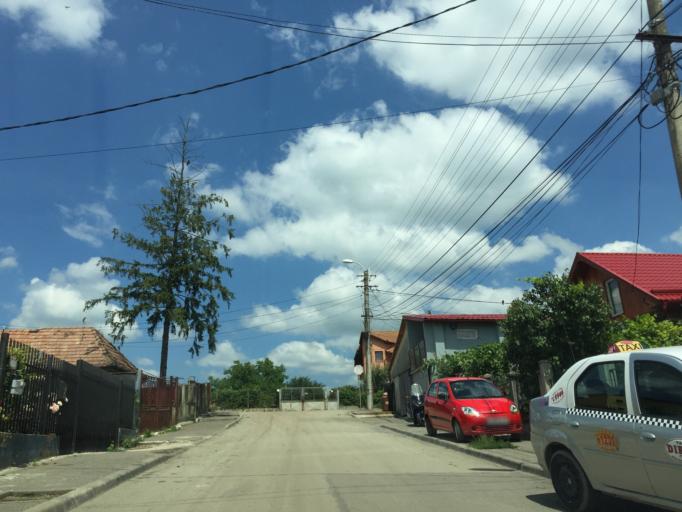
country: RO
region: Cluj
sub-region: Comuna Baciu
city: Baciu
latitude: 46.7920
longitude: 23.5617
